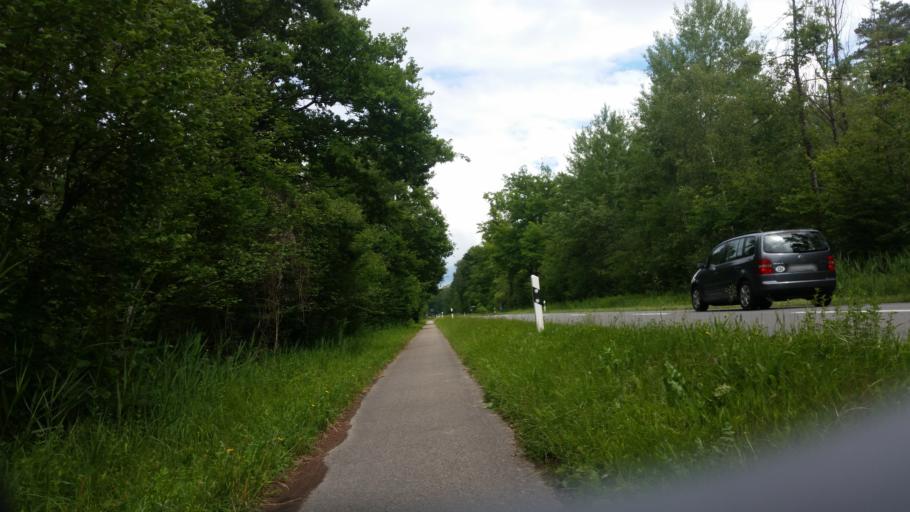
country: CH
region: Vaud
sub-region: Jura-Nord vaudois District
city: Yvonand
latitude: 46.8009
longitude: 6.7153
